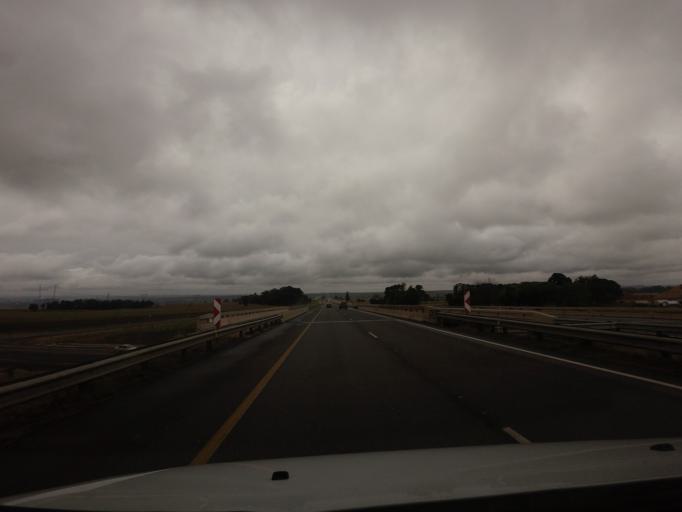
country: ZA
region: Mpumalanga
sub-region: Nkangala District Municipality
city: Middelburg
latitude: -25.8322
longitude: 29.4597
